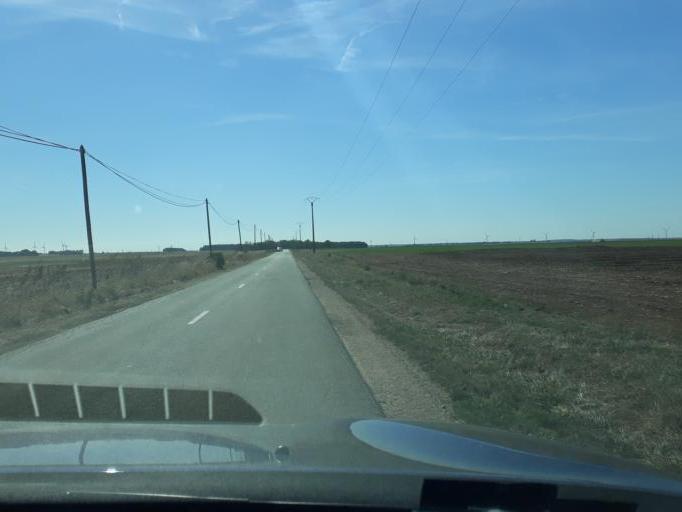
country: FR
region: Centre
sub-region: Departement du Loir-et-Cher
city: Ouzouer-le-Marche
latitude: 47.9406
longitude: 1.5205
